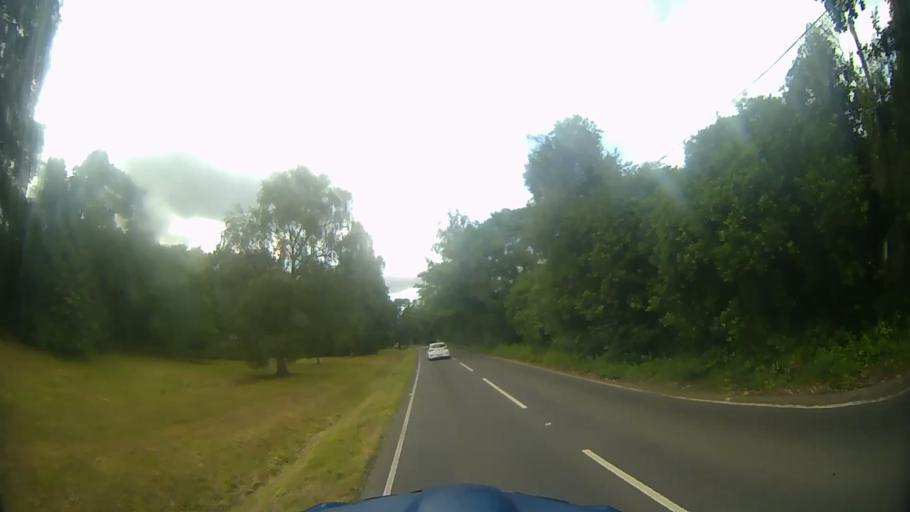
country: GB
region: England
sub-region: Wokingham
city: Barkham
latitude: 51.4121
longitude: -0.8757
